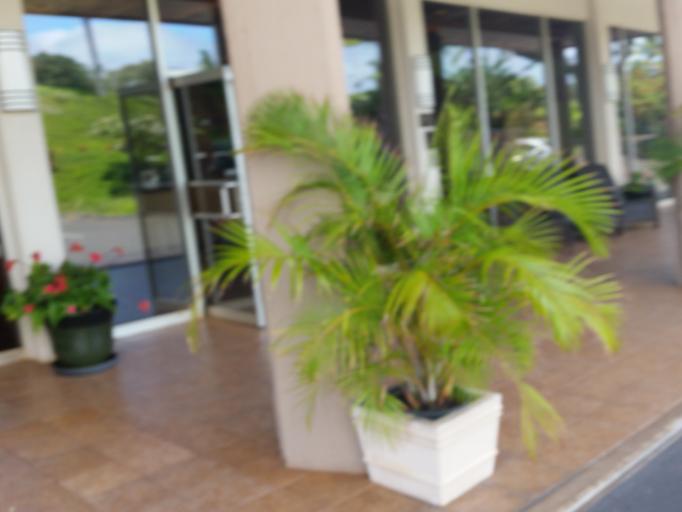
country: US
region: Hawaii
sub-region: Maui County
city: Ka'anapali
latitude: 20.9281
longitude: -156.6907
